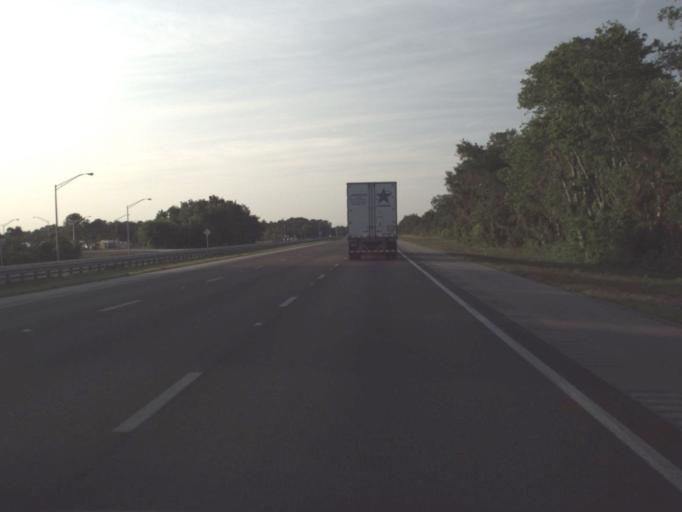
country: US
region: Florida
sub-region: Brevard County
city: Mims
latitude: 28.7051
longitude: -80.8855
